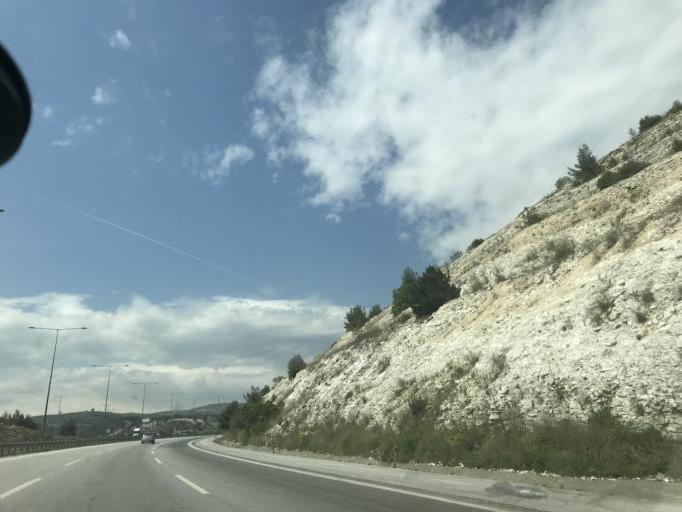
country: TR
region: Mersin
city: Tarsus
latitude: 37.1401
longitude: 34.8429
